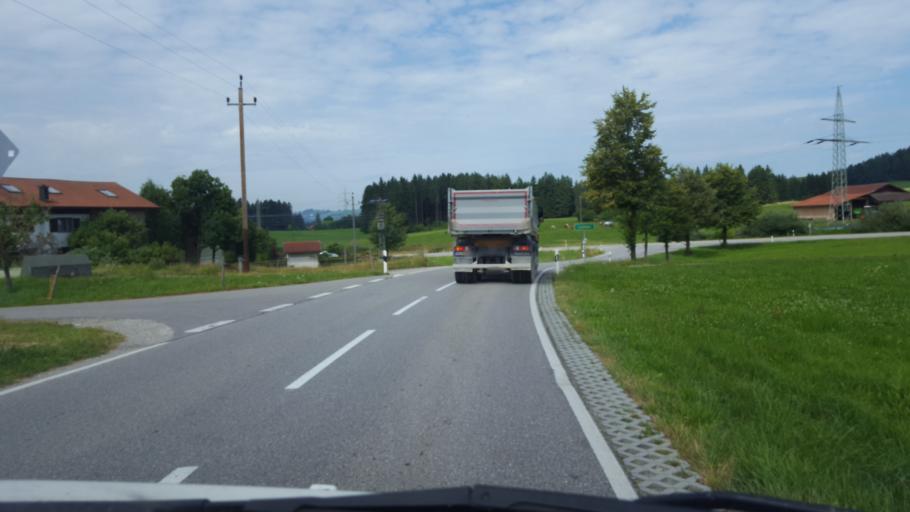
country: DE
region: Bavaria
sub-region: Swabia
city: Nesselwang
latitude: 47.6360
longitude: 10.5270
